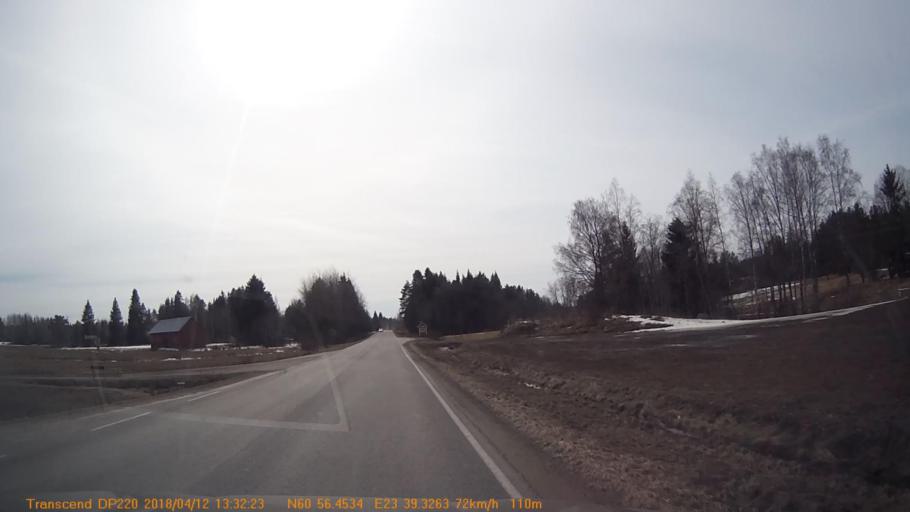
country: FI
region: Haeme
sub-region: Forssa
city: Forssa
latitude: 60.9407
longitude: 23.6553
